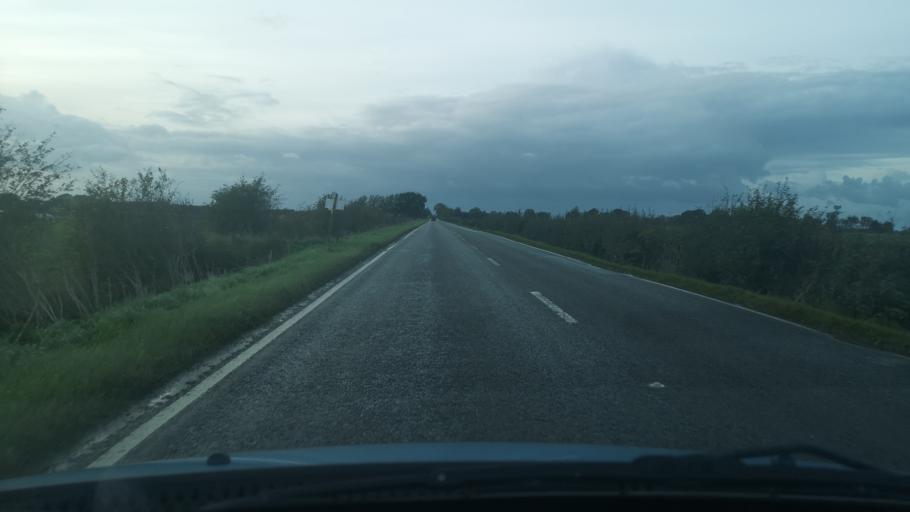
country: GB
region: England
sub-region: North Lincolnshire
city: Crowle
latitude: 53.5851
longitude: -0.9066
